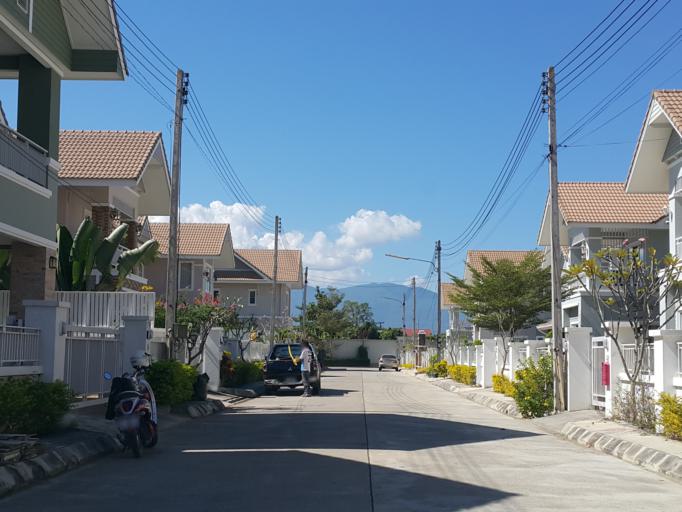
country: TH
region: Chiang Mai
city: San Sai
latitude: 18.8102
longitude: 99.0621
